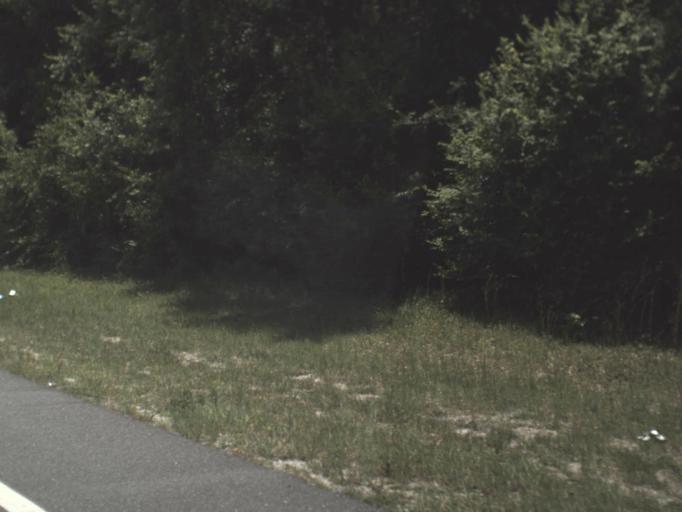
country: US
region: Florida
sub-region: Dixie County
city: Cross City
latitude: 29.6583
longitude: -82.9840
